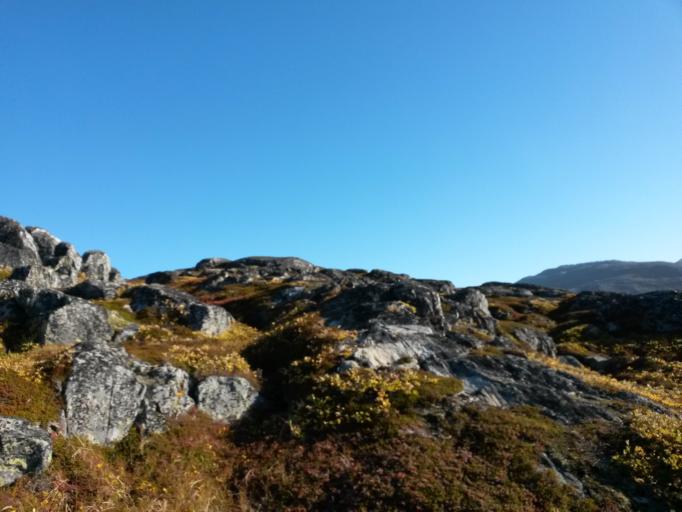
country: GL
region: Sermersooq
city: Nuuk
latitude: 64.1729
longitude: -51.7150
